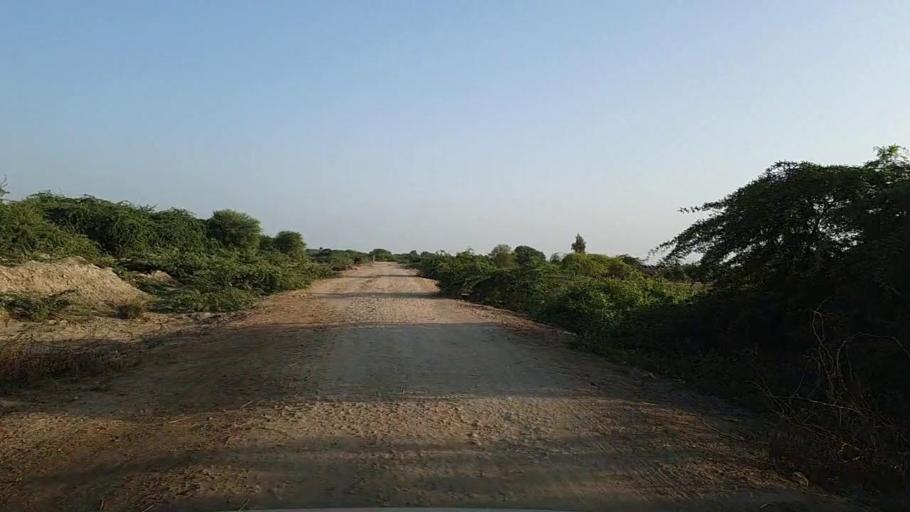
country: PK
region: Sindh
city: Kario
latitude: 24.7072
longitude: 68.6669
